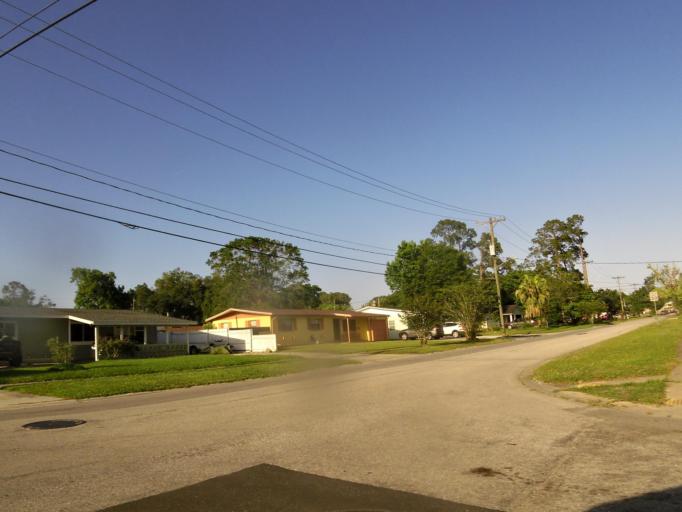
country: US
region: Florida
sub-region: Duval County
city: Jacksonville
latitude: 30.2783
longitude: -81.6071
